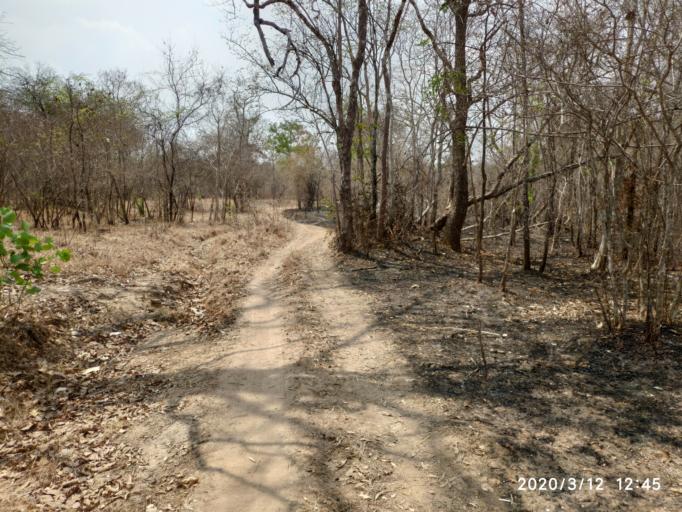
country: KH
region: Preah Vihear
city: Tbeng Meanchey
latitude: 13.7838
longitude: 104.5360
